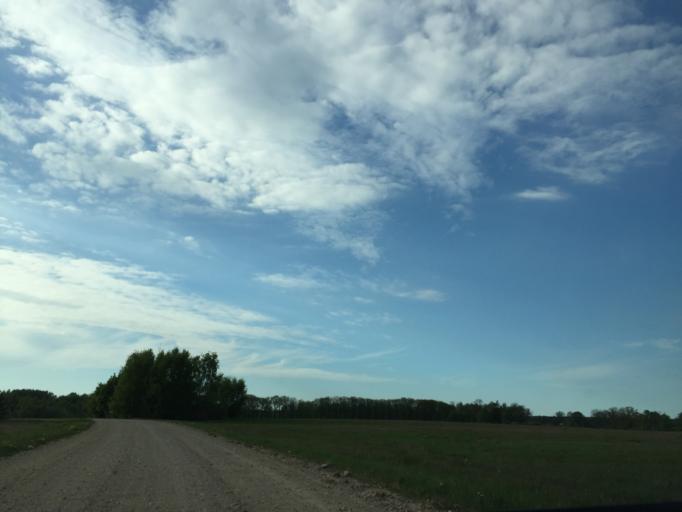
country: LV
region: Limbazu Rajons
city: Limbazi
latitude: 57.3722
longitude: 24.6892
